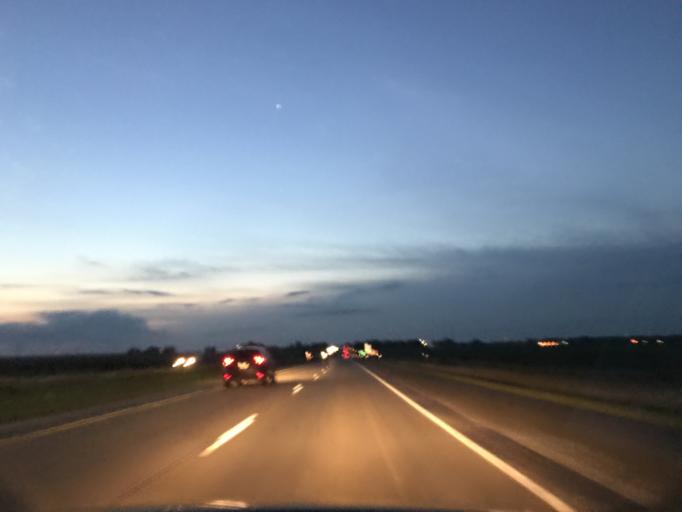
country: US
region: Iowa
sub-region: Polk County
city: Mitchellville
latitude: 41.6803
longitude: -93.3850
